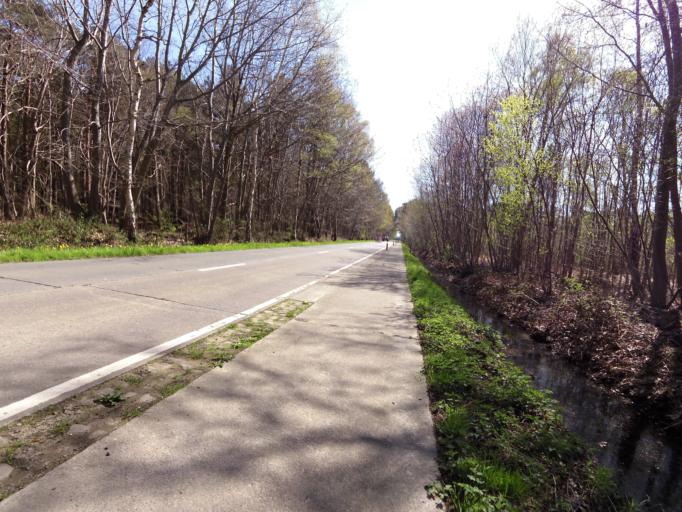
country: BE
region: Flanders
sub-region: Provincie West-Vlaanderen
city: Jabbeke
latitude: 51.1569
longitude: 3.0862
